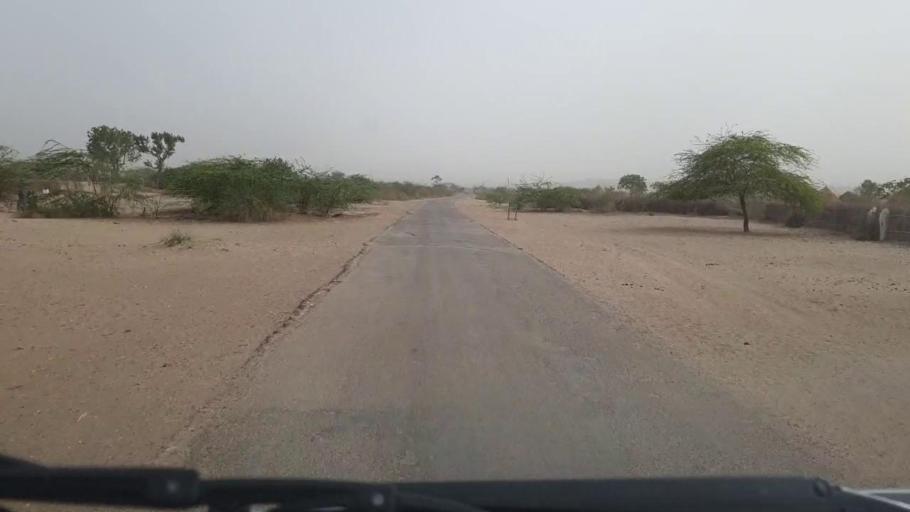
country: PK
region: Sindh
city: Islamkot
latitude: 25.0717
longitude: 70.5633
